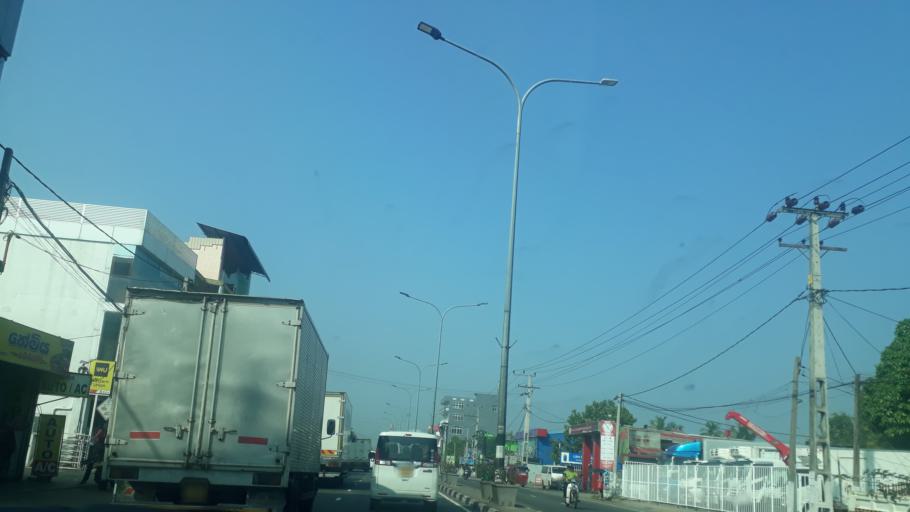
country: LK
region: Western
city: Kelaniya
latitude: 6.9694
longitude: 79.9127
